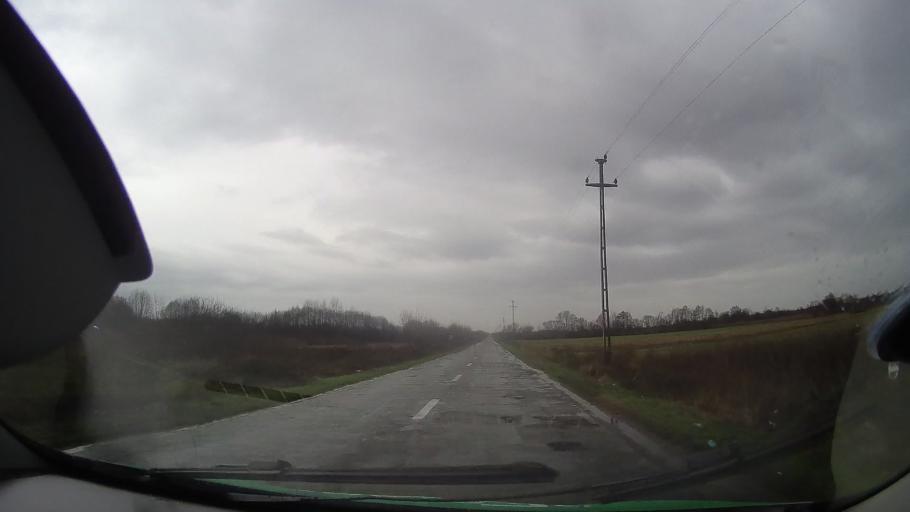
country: RO
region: Bihor
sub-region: Comuna Soimi
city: Soimi
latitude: 46.6844
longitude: 22.1113
